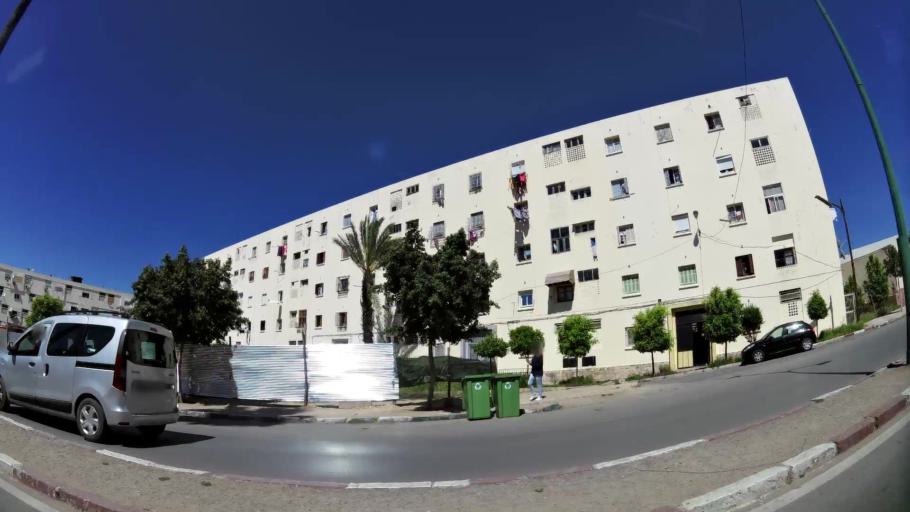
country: MA
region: Meknes-Tafilalet
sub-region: Meknes
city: Meknes
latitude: 33.8889
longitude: -5.5689
